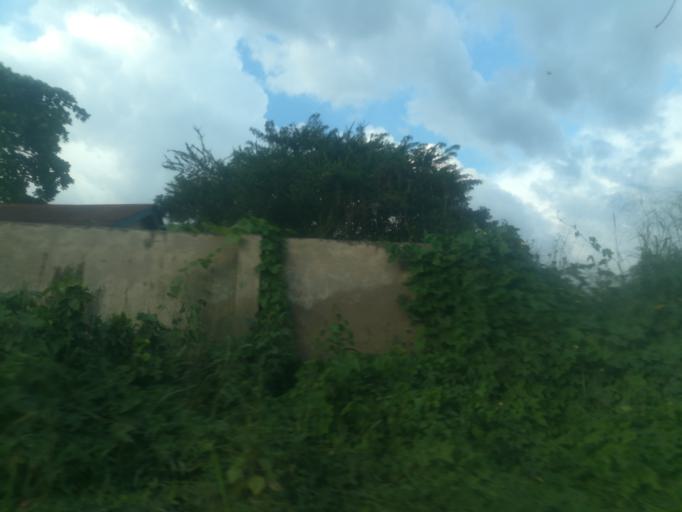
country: NG
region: Oyo
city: Ibadan
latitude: 7.3801
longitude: 3.8424
